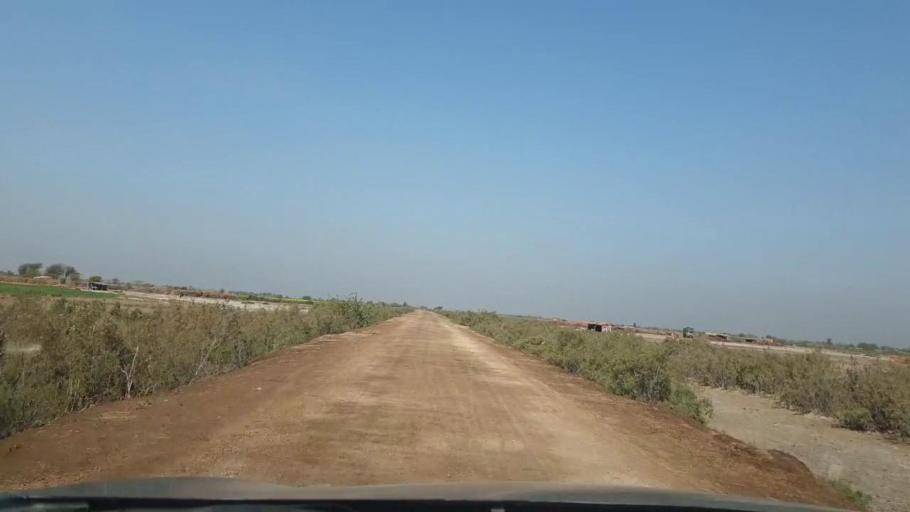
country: PK
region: Sindh
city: Berani
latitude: 25.7028
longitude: 68.8676
